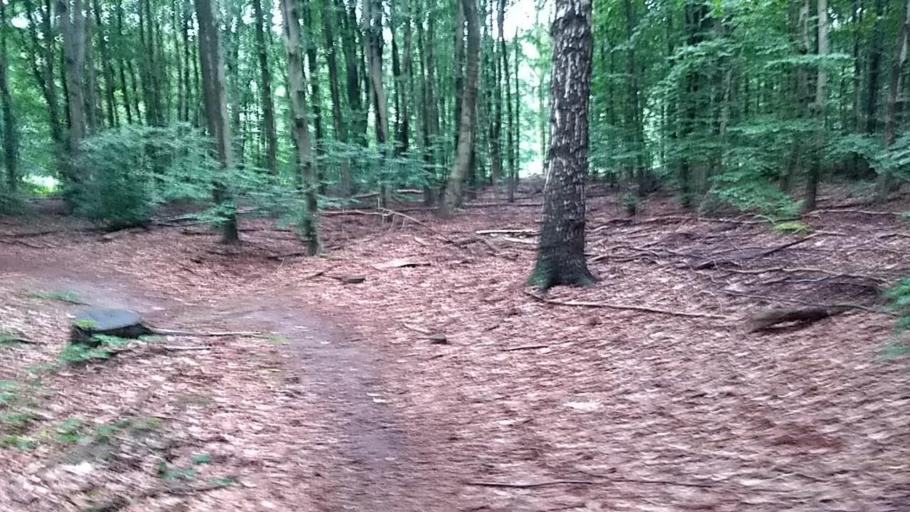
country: NL
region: Overijssel
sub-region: Gemeente Steenwijkerland
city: Vollenhove
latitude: 52.6664
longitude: 5.9338
